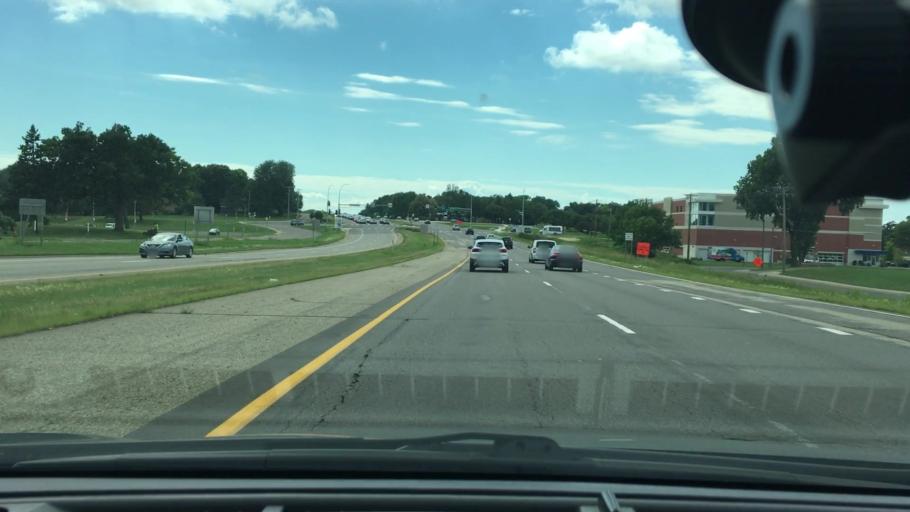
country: US
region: Minnesota
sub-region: Hennepin County
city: Golden Valley
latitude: 44.9848
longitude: -93.3569
